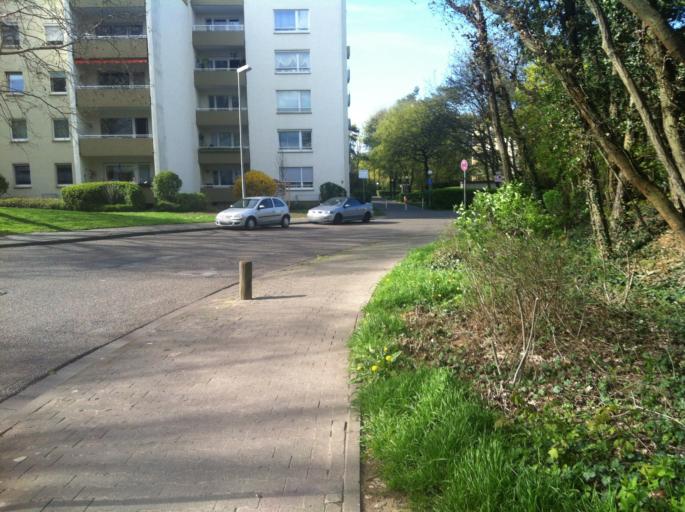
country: DE
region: Rheinland-Pfalz
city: Budenheim
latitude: 50.0082
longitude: 8.2054
